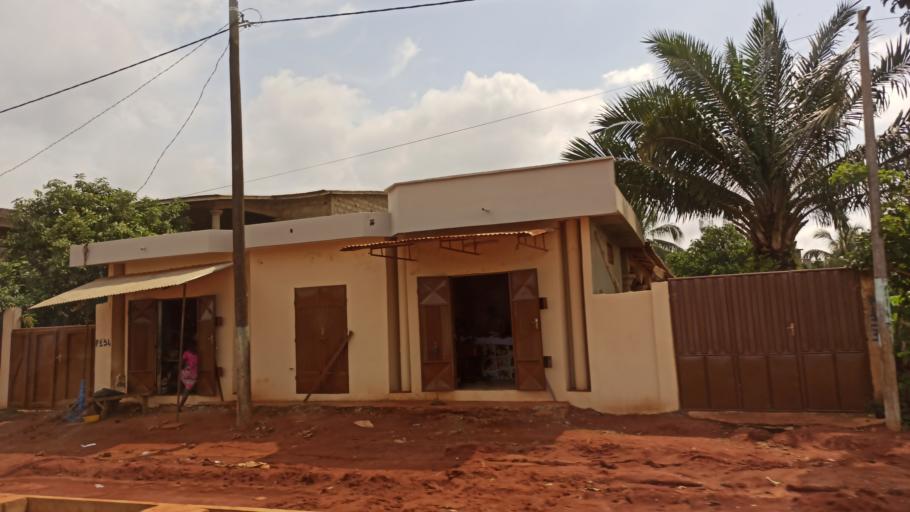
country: BJ
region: Queme
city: Porto-Novo
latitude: 6.4924
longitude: 2.5892
